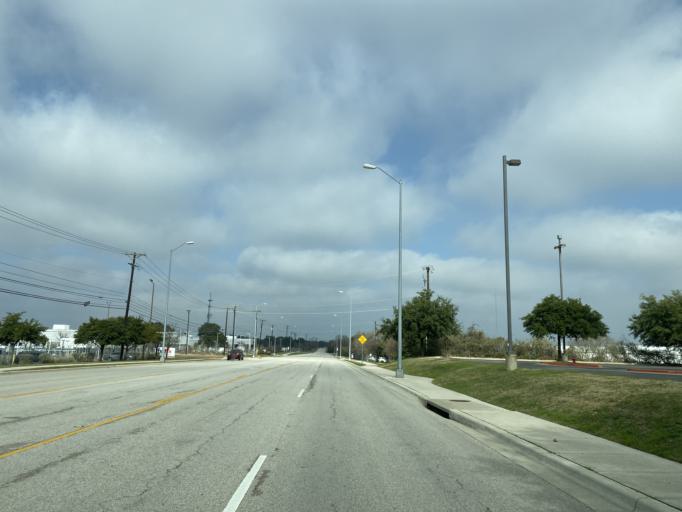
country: US
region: Texas
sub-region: Williamson County
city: Round Rock
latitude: 30.5407
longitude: -97.6948
